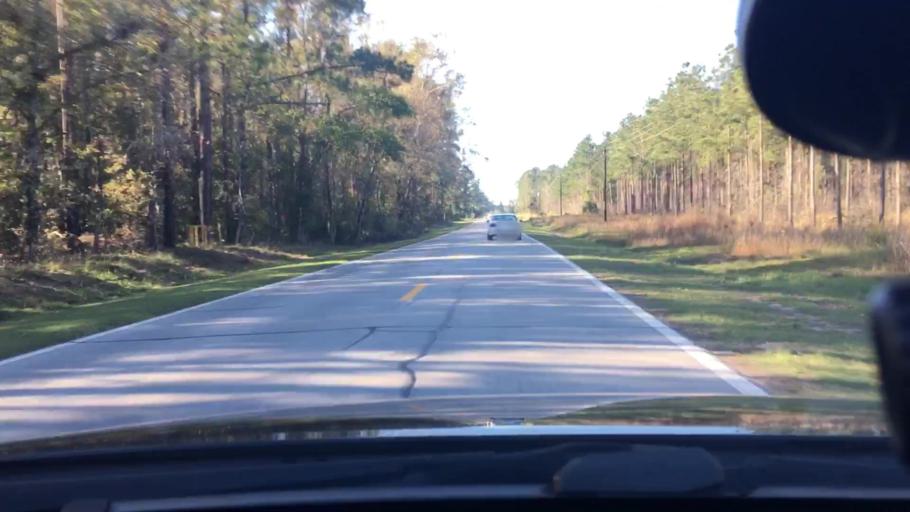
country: US
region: North Carolina
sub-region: Craven County
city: Vanceboro
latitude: 35.2250
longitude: -77.1305
